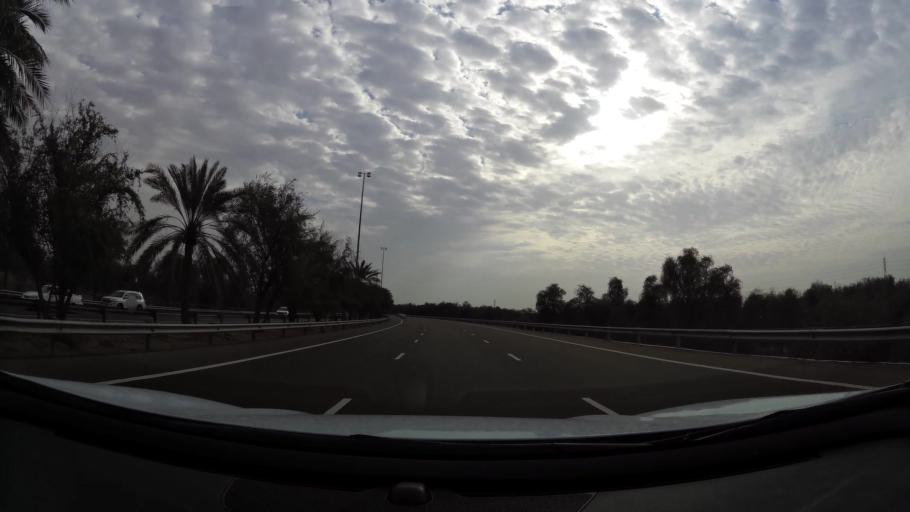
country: AE
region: Abu Dhabi
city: Al Ain
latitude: 24.1673
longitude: 55.2714
